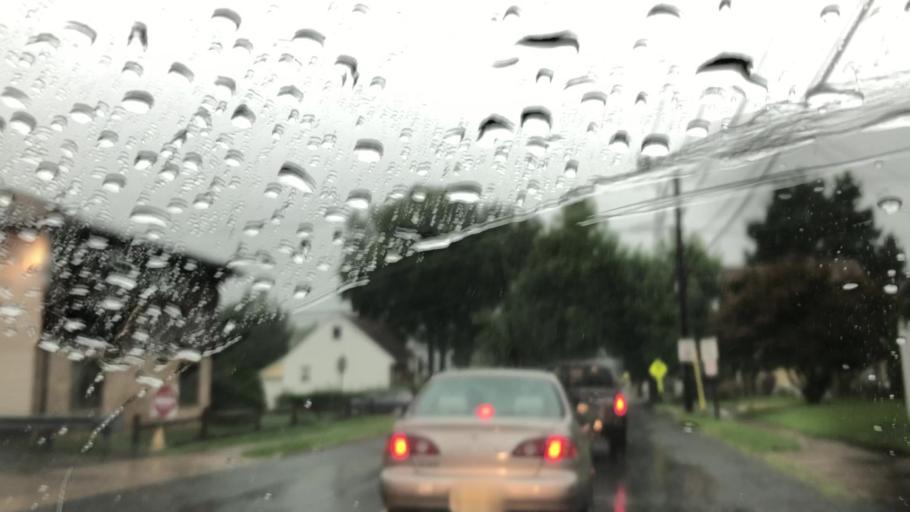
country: US
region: New Jersey
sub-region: Bergen County
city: Elmwood Park
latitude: 40.9209
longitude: -74.1172
